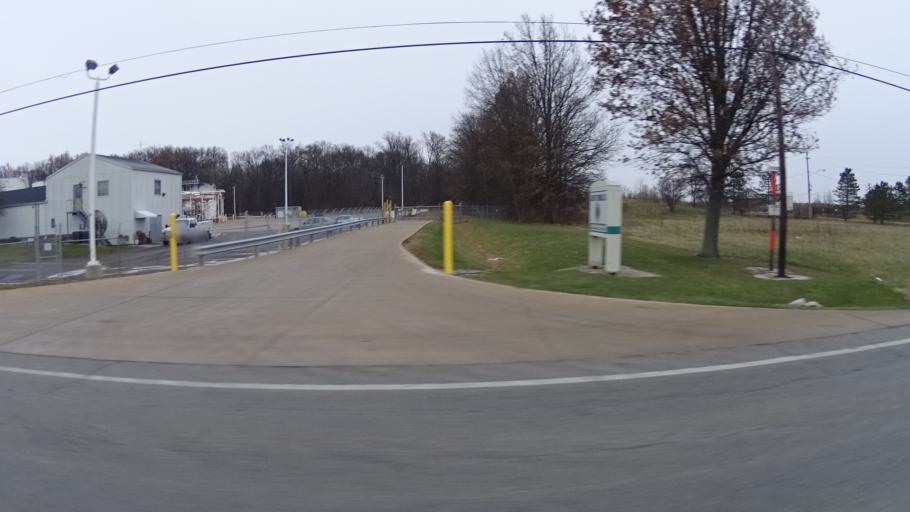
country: US
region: Ohio
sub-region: Lorain County
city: Eaton Estates
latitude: 41.3050
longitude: -82.0209
